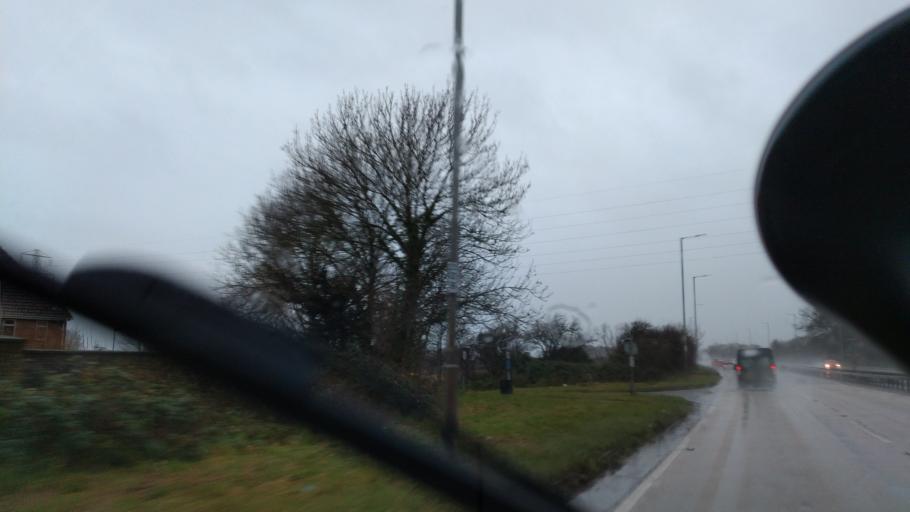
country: GB
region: England
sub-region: West Sussex
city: Lancing
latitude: 50.8377
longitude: -0.3423
